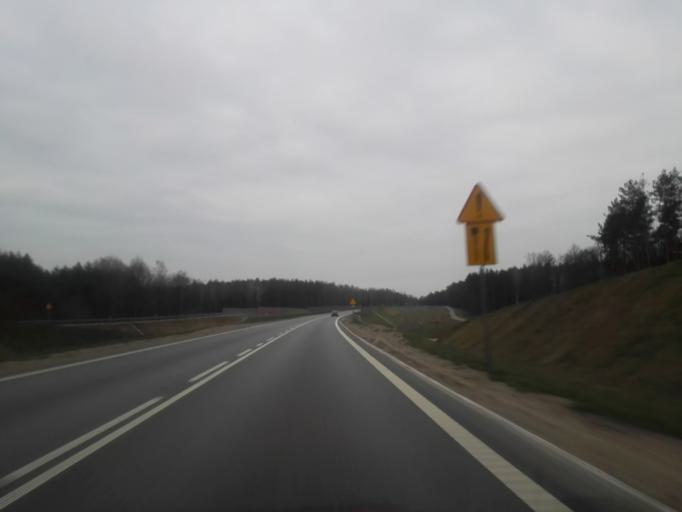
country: PL
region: Podlasie
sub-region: Powiat kolnenski
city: Stawiski
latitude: 53.3583
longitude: 22.1609
